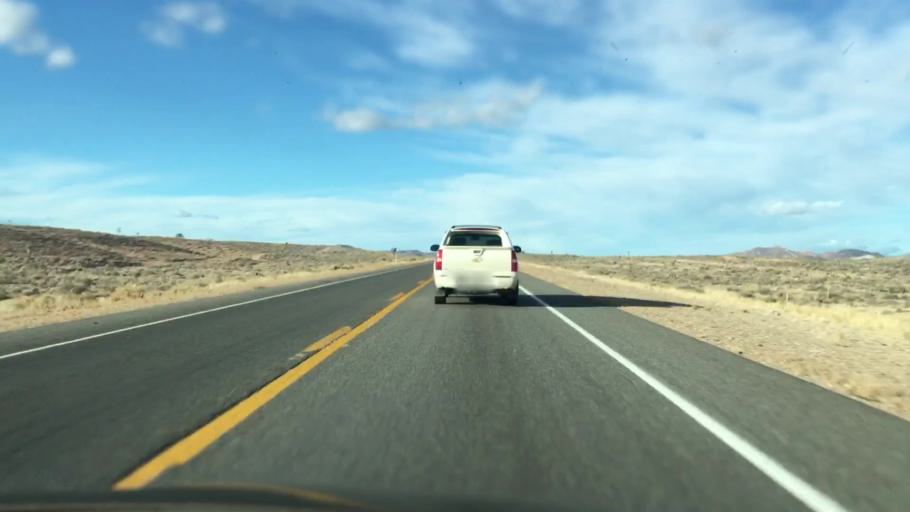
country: US
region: Nevada
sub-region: Esmeralda County
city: Goldfield
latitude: 37.5634
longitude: -117.1993
